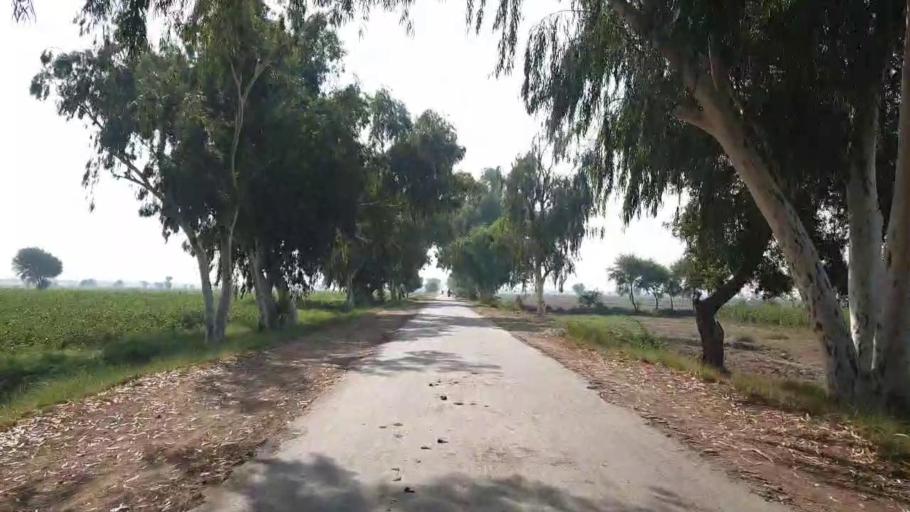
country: PK
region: Sindh
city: Shahdadpur
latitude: 25.9354
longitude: 68.7289
